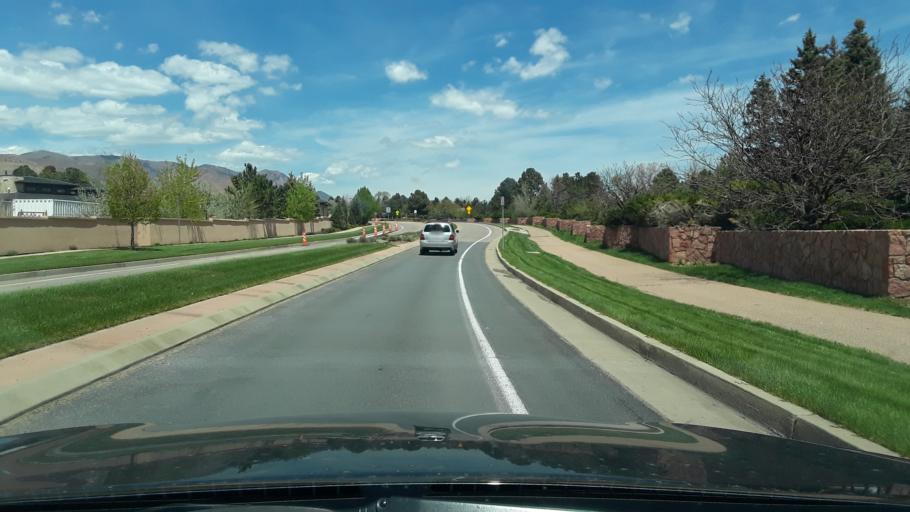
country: US
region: Colorado
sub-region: El Paso County
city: Manitou Springs
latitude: 38.8759
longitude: -104.8651
